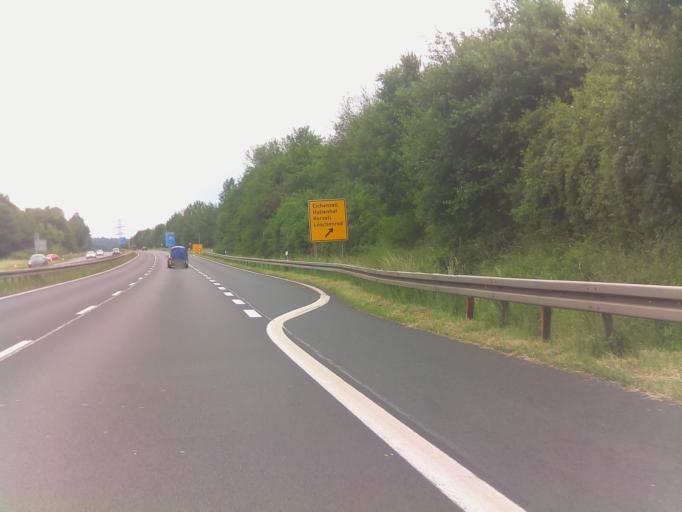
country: DE
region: Hesse
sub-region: Regierungsbezirk Kassel
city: Eichenzell
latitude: 50.4977
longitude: 9.6852
